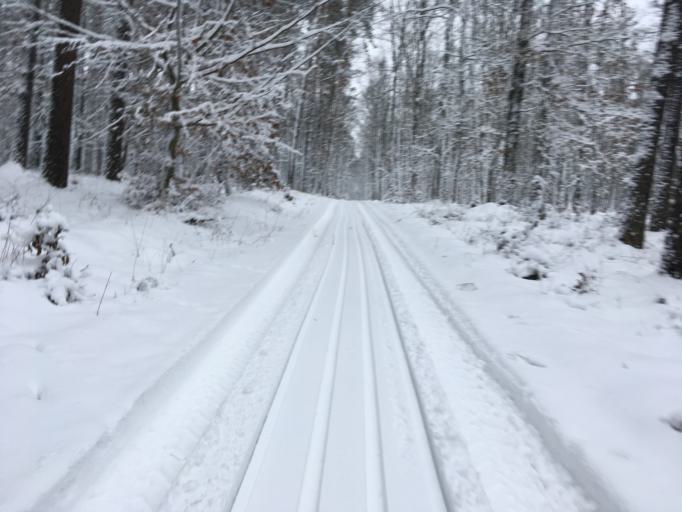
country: PL
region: Kujawsko-Pomorskie
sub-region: Powiat brodnicki
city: Gorzno
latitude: 53.1954
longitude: 19.6897
